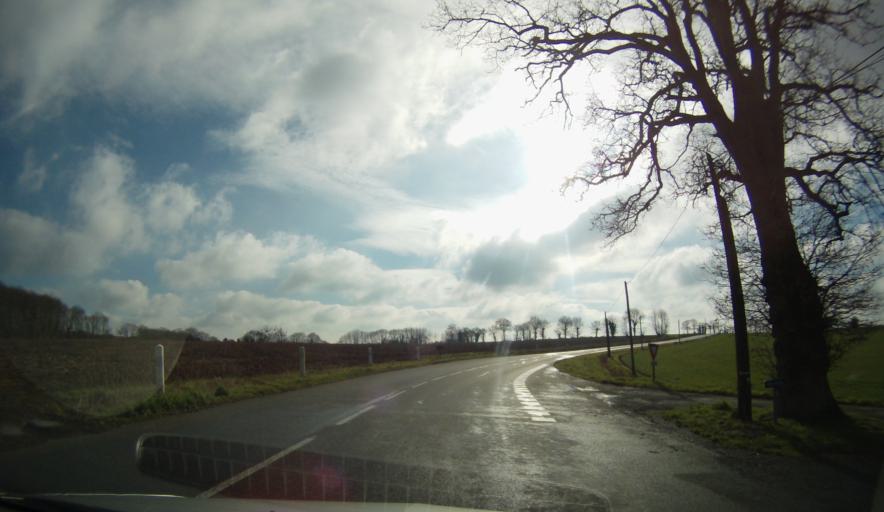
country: FR
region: Brittany
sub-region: Departement d'Ille-et-Vilaine
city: Corps-Nuds
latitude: 47.9697
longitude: -1.5833
